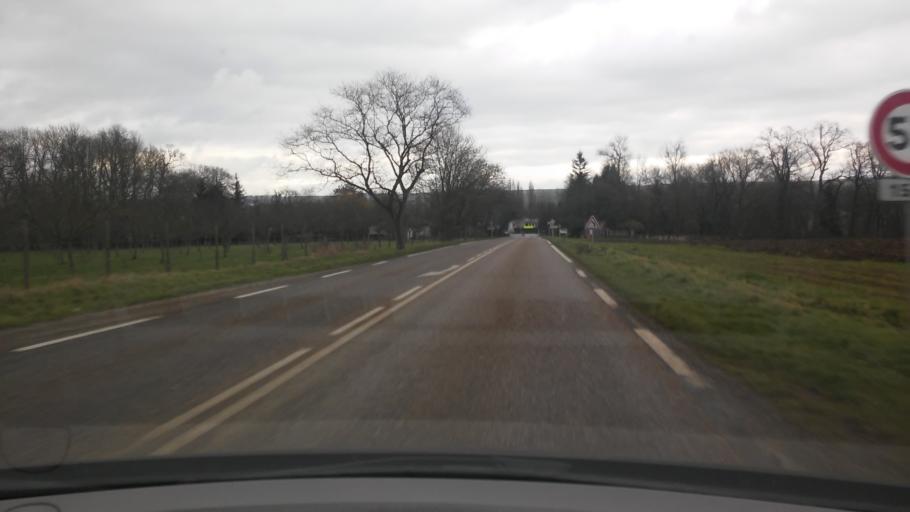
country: FR
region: Lorraine
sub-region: Departement de la Moselle
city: Courcelles-Chaussy
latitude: 49.1100
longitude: 6.3780
